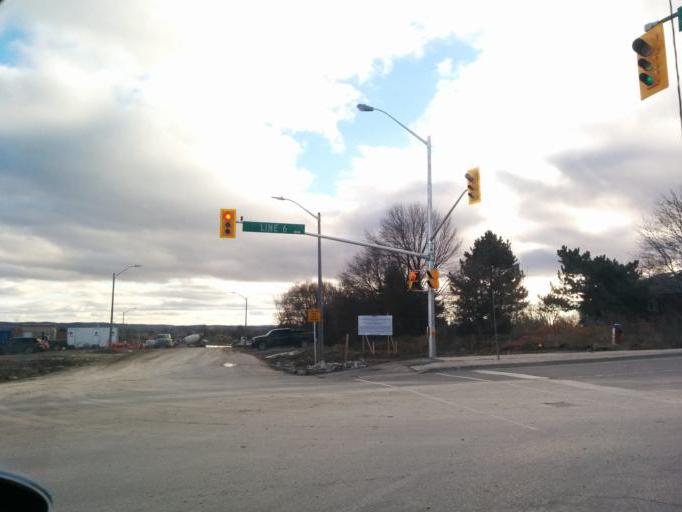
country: CA
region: Ontario
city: Bradford West Gwillimbury
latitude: 44.0988
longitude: -79.5761
